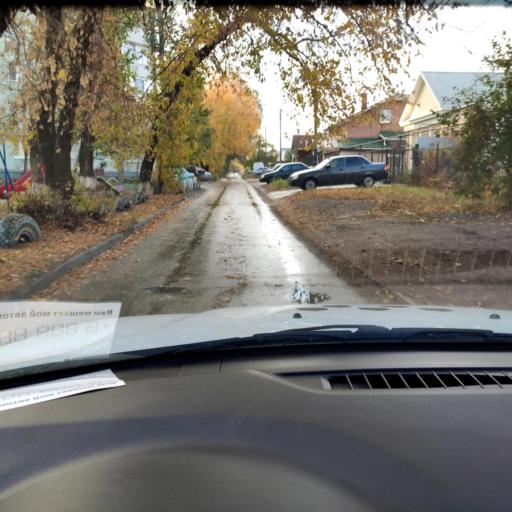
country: RU
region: Samara
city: Tol'yatti
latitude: 53.5371
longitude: 49.4084
